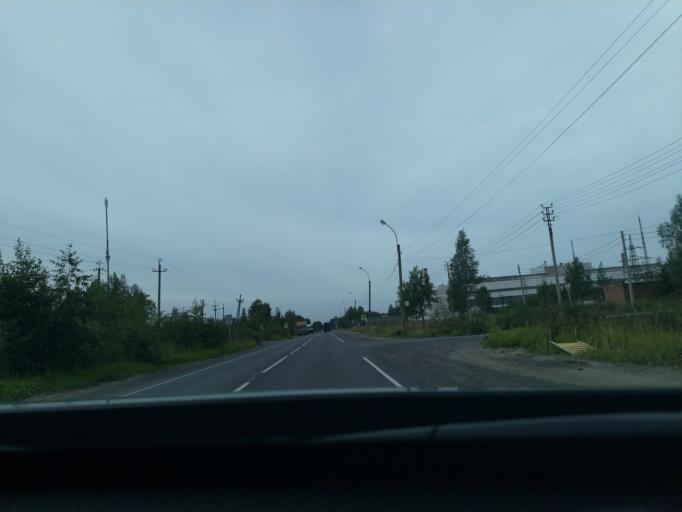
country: RU
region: Leningrad
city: Nikol'skoye
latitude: 59.7256
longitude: 30.7780
